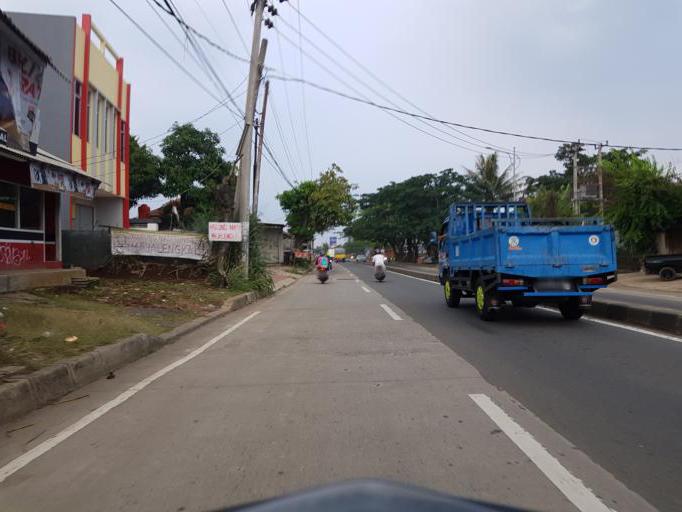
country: ID
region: West Java
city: Ciampea
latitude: -6.5042
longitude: 106.7578
